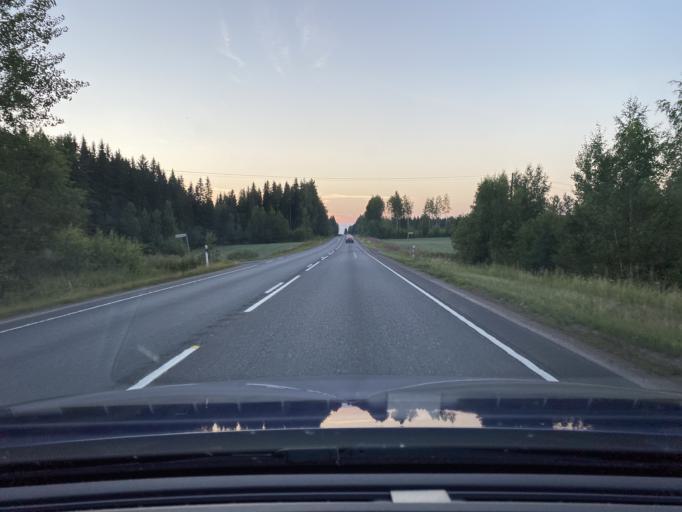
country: FI
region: Pirkanmaa
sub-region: Luoteis-Pirkanmaa
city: Ikaalinen
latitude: 61.8304
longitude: 22.9428
